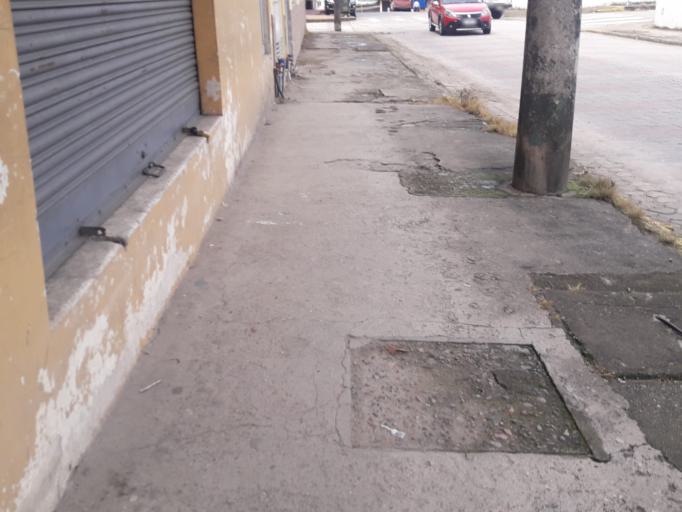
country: EC
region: Napo
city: Tena
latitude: -0.9891
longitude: -77.8149
